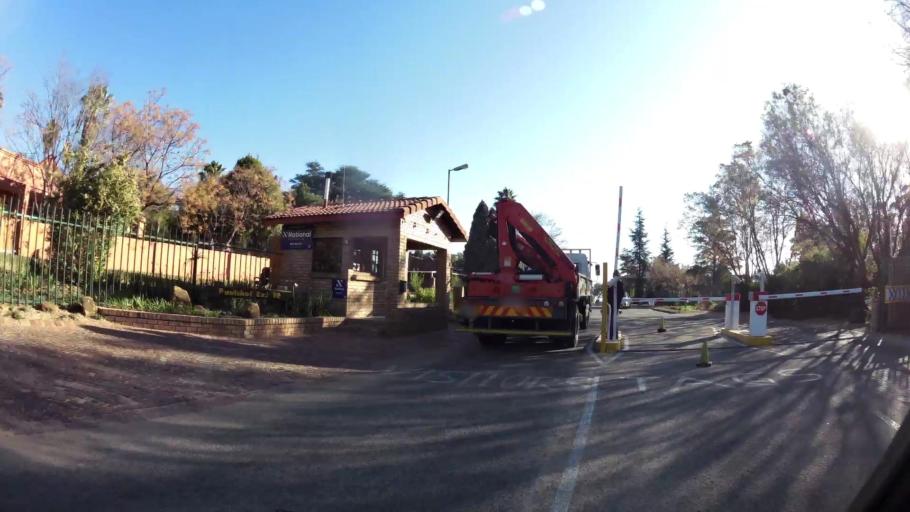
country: ZA
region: Gauteng
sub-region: City of Johannesburg Metropolitan Municipality
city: Midrand
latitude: -26.0273
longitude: 28.0491
